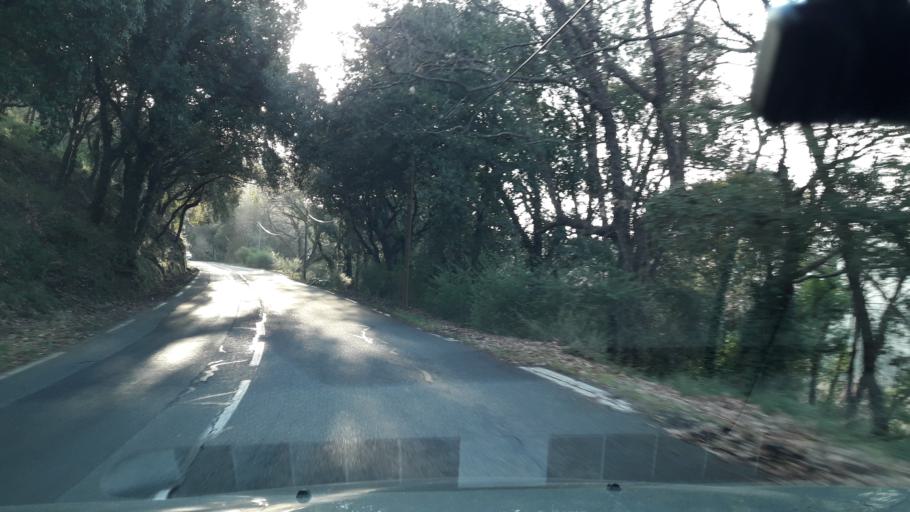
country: FR
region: Provence-Alpes-Cote d'Azur
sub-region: Departement du Var
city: Tanneron
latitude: 43.5191
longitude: 6.8413
